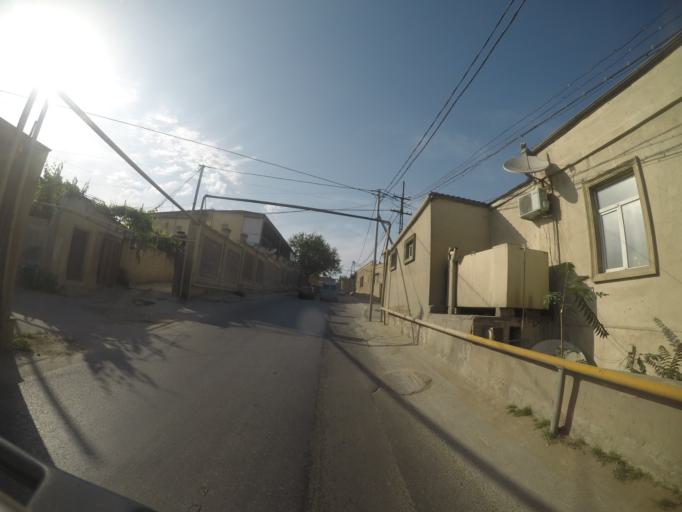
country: AZ
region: Baki
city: Binagadi
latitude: 40.4666
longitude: 49.8419
